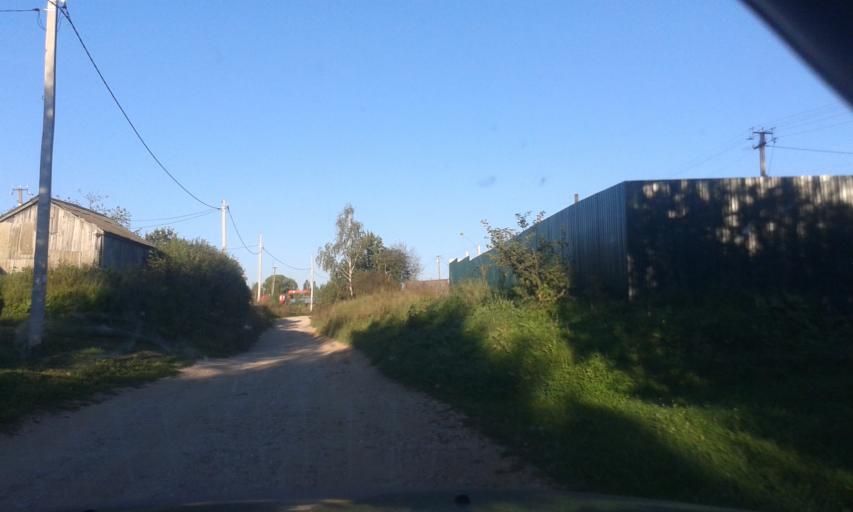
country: RU
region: Tula
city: Krapivna
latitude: 54.1351
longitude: 37.1552
